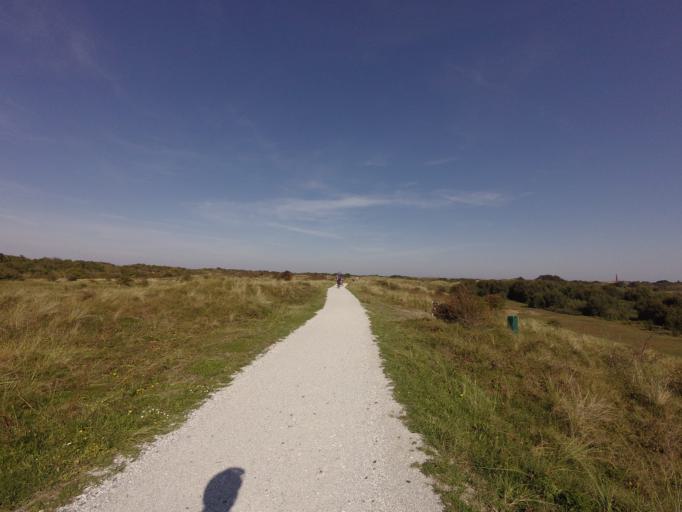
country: NL
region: Friesland
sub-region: Gemeente Schiermonnikoog
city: Schiermonnikoog
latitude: 53.4744
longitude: 6.1408
